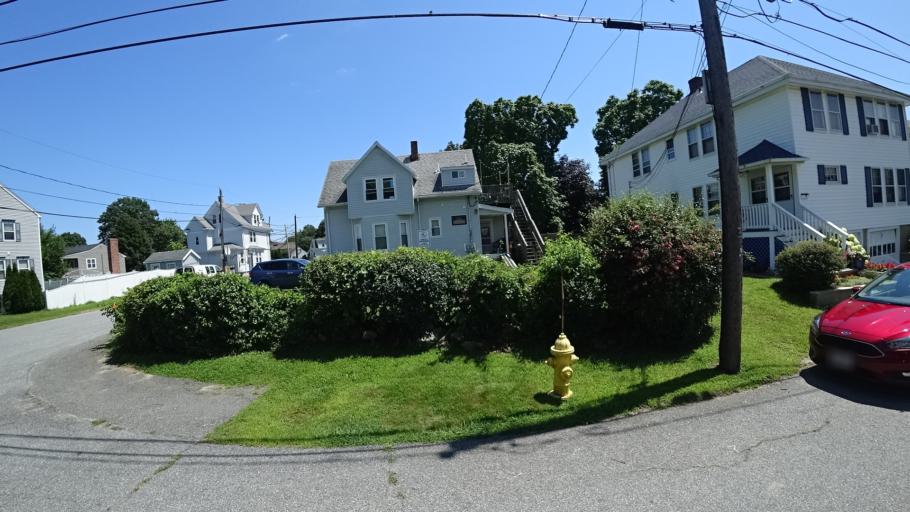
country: US
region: Massachusetts
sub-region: Norfolk County
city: Dedham
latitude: 42.2638
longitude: -71.1806
